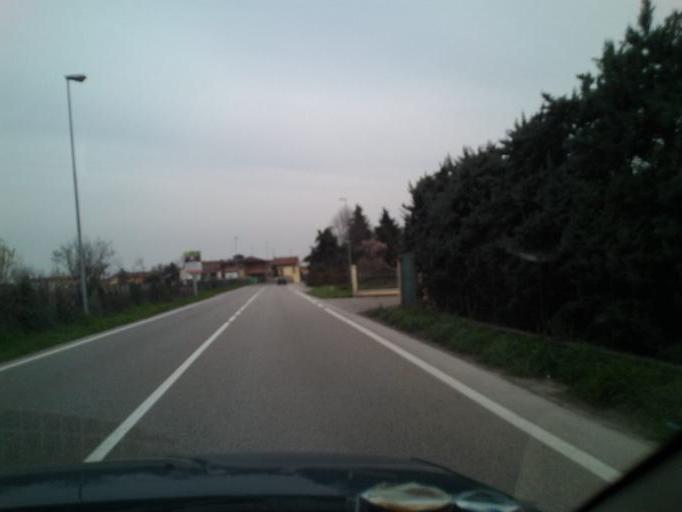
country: IT
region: Veneto
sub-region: Provincia di Verona
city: Mozzecane
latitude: 45.3235
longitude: 10.8314
